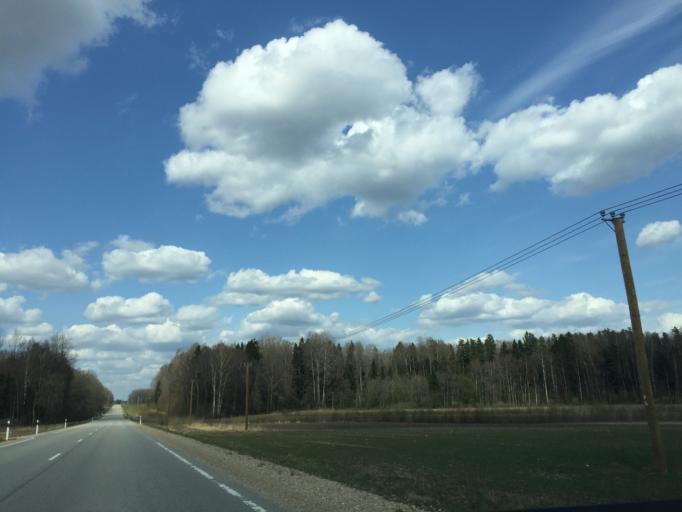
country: LV
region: Skriveri
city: Skriveri
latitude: 56.7740
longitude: 25.1662
